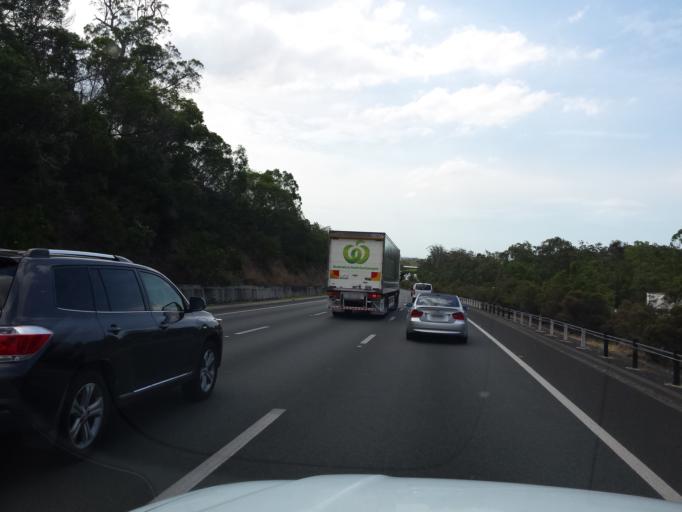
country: AU
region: Queensland
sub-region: Gold Coast
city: Nerang
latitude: -27.9683
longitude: 153.3469
